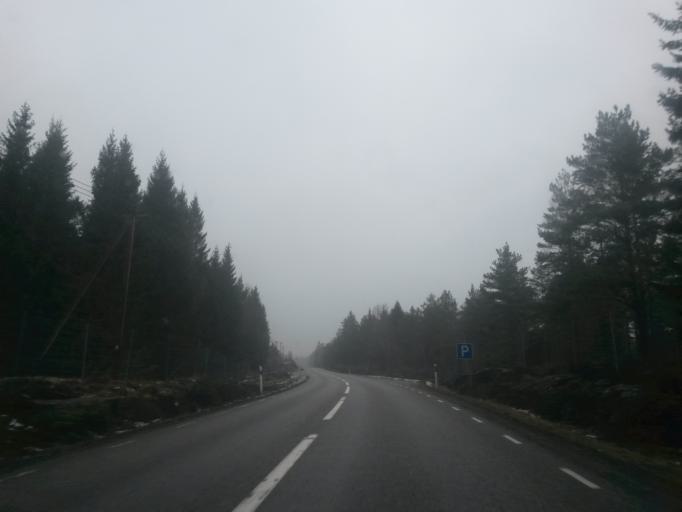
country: SE
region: Vaestra Goetaland
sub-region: Alingsas Kommun
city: Sollebrunn
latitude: 58.1921
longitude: 12.4315
